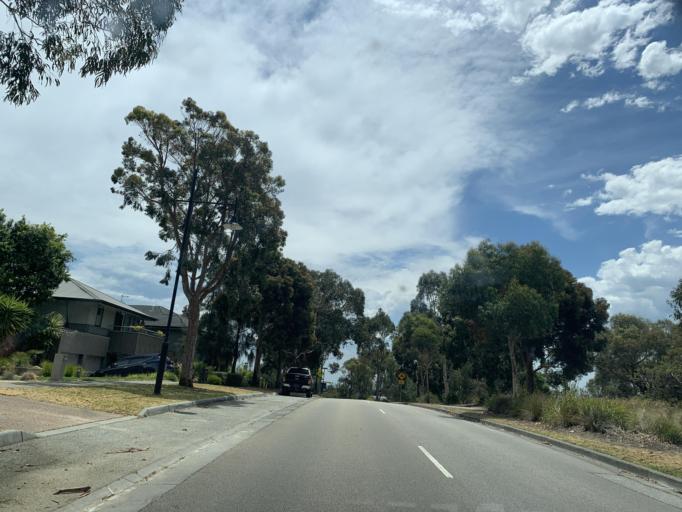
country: AU
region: Victoria
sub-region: Casey
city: Cranbourne South
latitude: -38.1330
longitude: 145.2543
